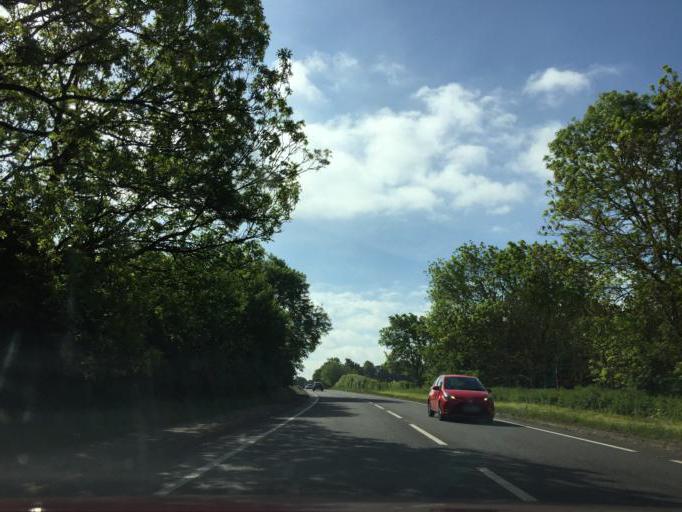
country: GB
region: England
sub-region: Northamptonshire
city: Towcester
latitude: 52.1114
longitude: -0.9515
